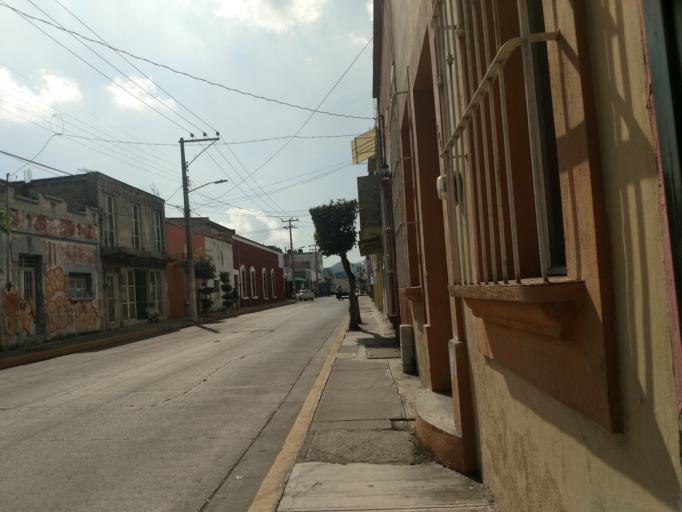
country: MX
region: Nayarit
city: Tepic
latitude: 21.5129
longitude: -104.8889
